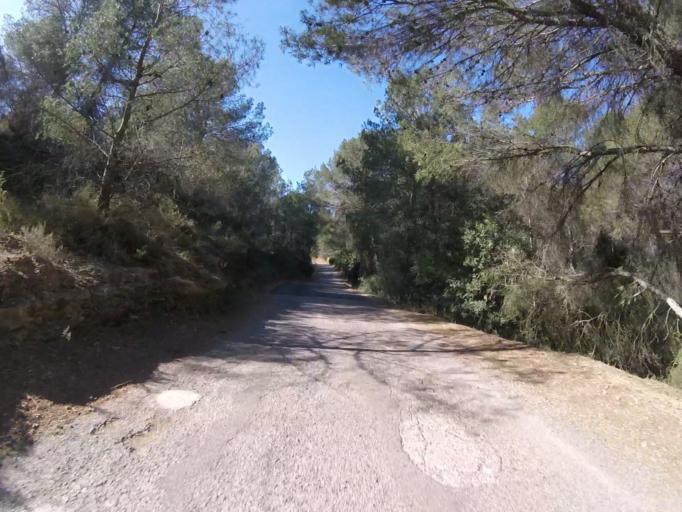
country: ES
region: Valencia
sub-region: Provincia de Castello
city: Orpesa/Oropesa del Mar
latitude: 40.0815
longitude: 0.1199
